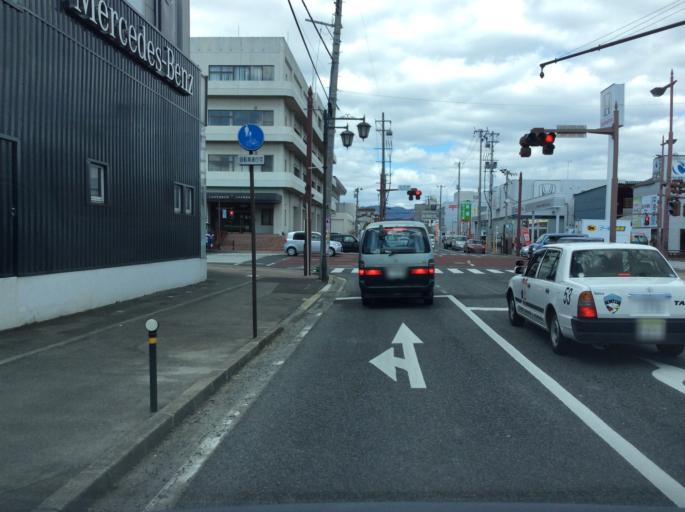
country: JP
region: Fukushima
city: Iwaki
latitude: 37.0536
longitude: 140.9004
